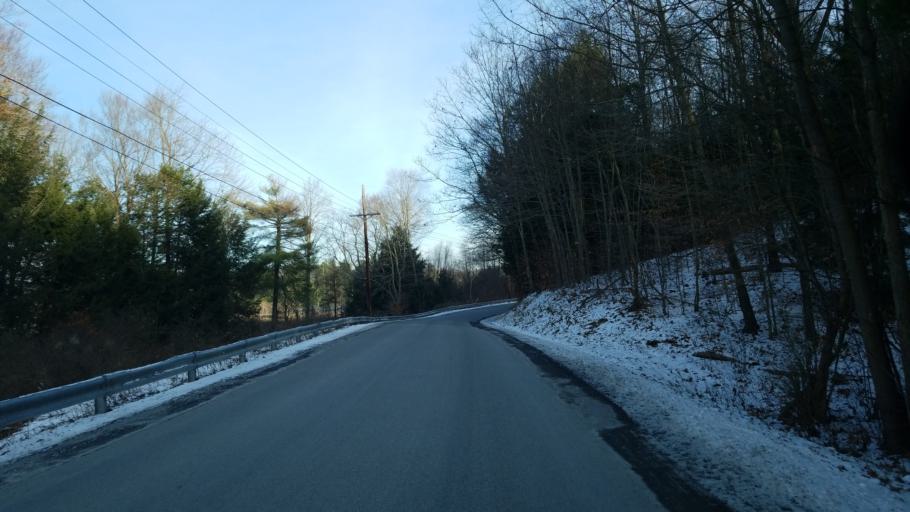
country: US
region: Pennsylvania
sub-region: Clearfield County
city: DuBois
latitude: 41.1210
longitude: -78.7135
